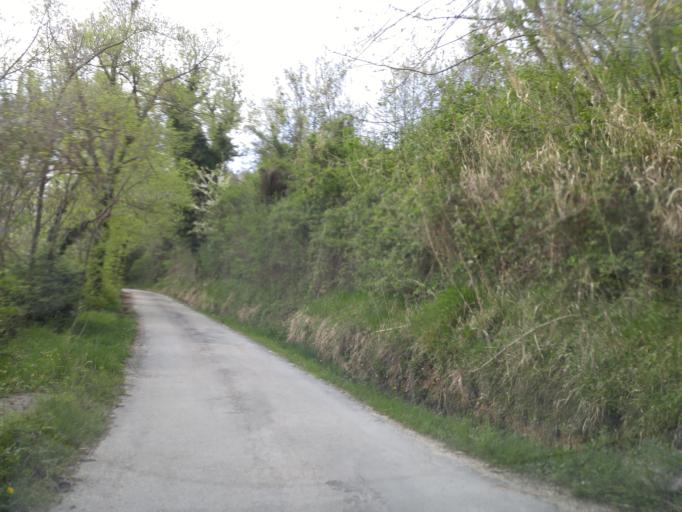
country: IT
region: The Marches
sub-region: Provincia di Pesaro e Urbino
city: Acqualagna
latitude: 43.6490
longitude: 12.6891
